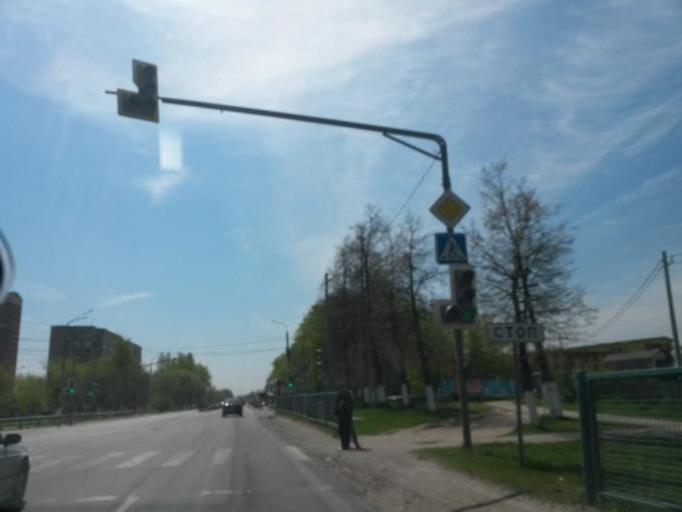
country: RU
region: Moskovskaya
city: Shcherbinka
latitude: 55.4739
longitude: 37.5631
